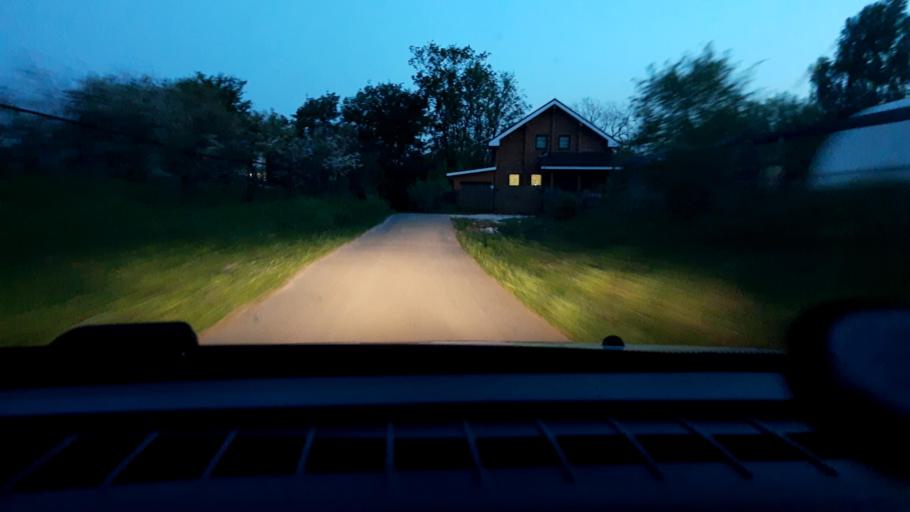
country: RU
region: Nizjnij Novgorod
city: Burevestnik
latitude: 56.0370
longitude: 43.7240
